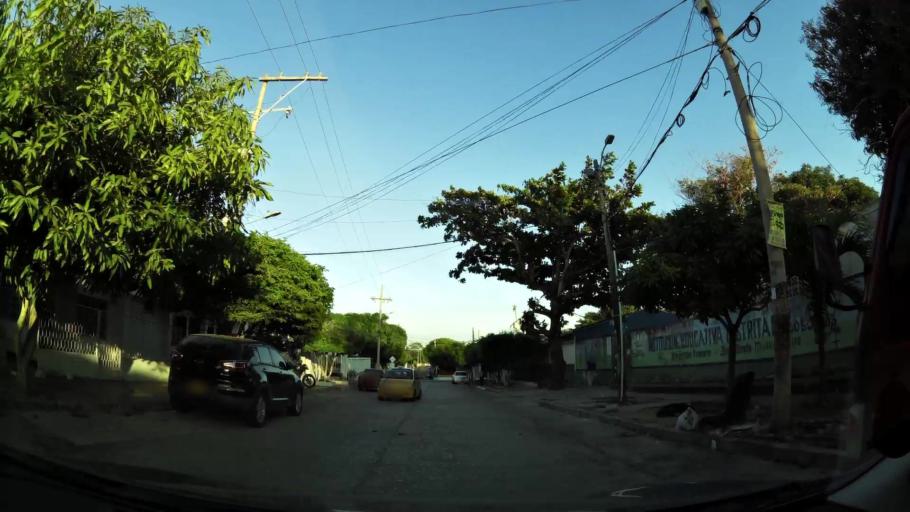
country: CO
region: Atlantico
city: Barranquilla
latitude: 10.9748
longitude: -74.7992
